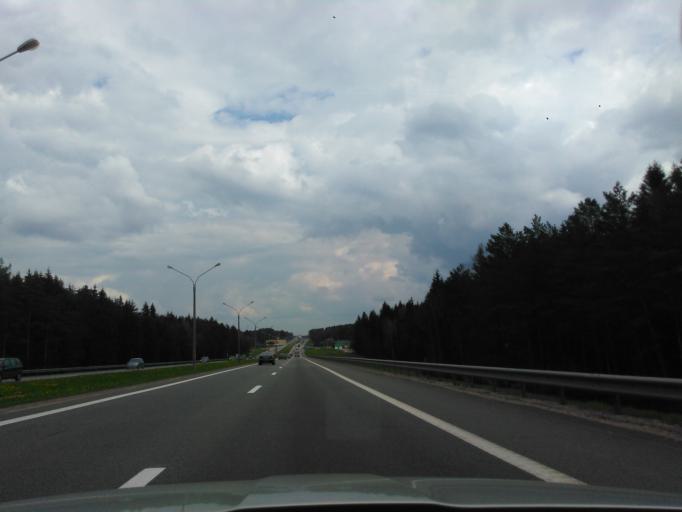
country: BY
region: Minsk
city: Kalodzishchy
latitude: 53.9726
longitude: 27.7581
